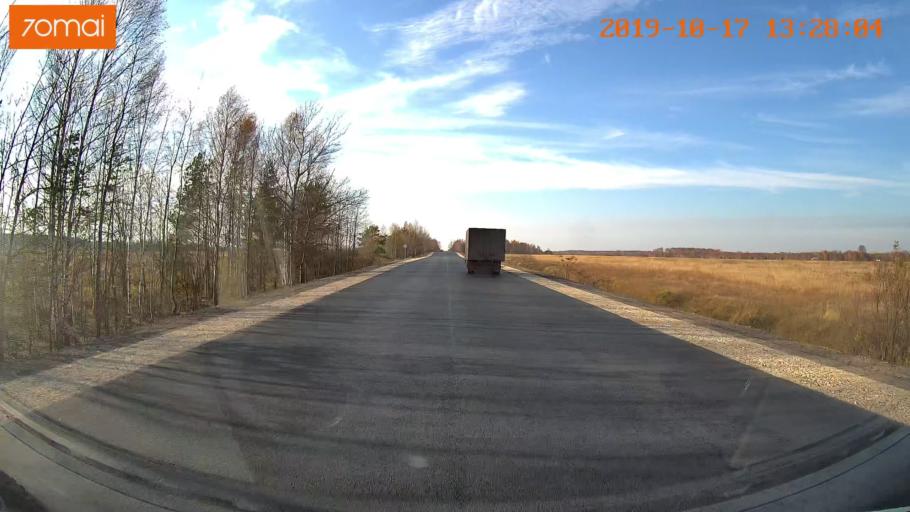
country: RU
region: Vladimir
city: Velikodvorskiy
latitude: 55.1150
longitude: 40.8793
